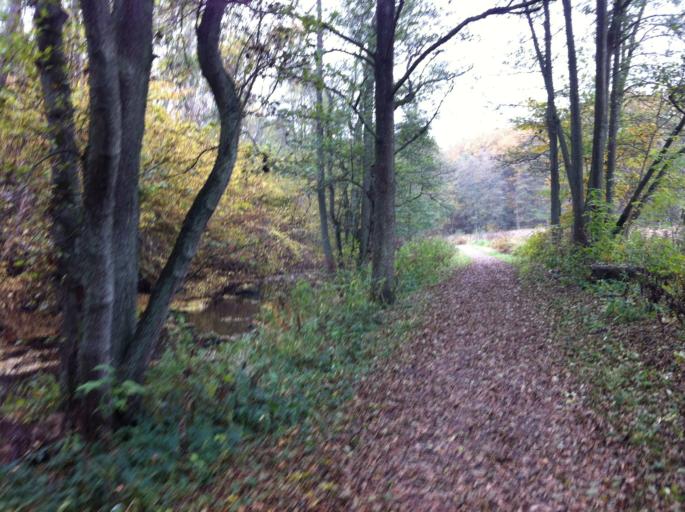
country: SE
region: Skane
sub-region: Helsingborg
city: Gantofta
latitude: 55.9939
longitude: 12.8032
